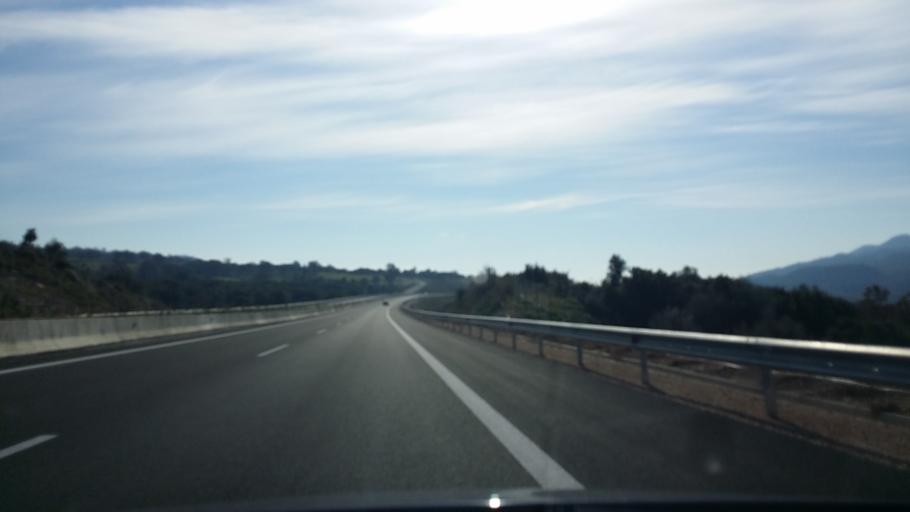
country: GR
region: West Greece
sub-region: Nomos Aitolias kai Akarnanias
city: Fitiai
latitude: 38.7269
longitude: 21.2129
